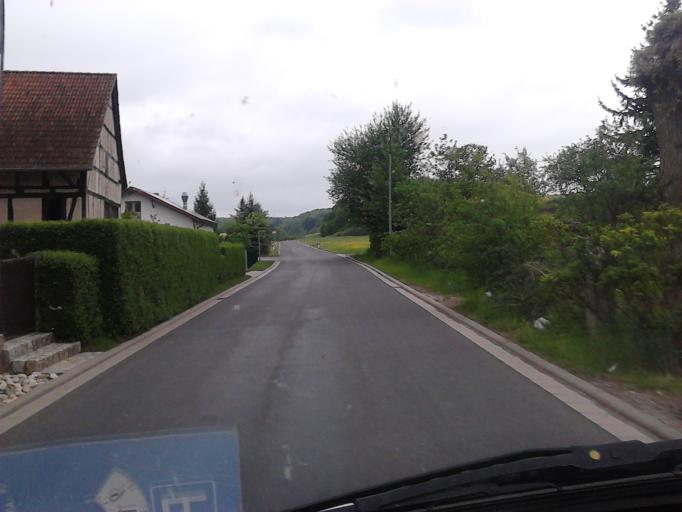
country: DE
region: Thuringia
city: Hellingen
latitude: 50.2509
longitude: 10.6851
